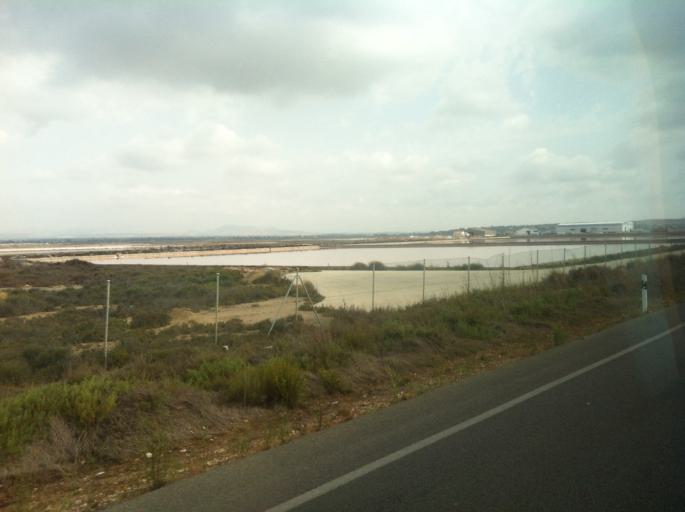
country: ES
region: Valencia
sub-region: Provincia de Alicante
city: Santa Pola
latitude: 38.1879
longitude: -0.6004
